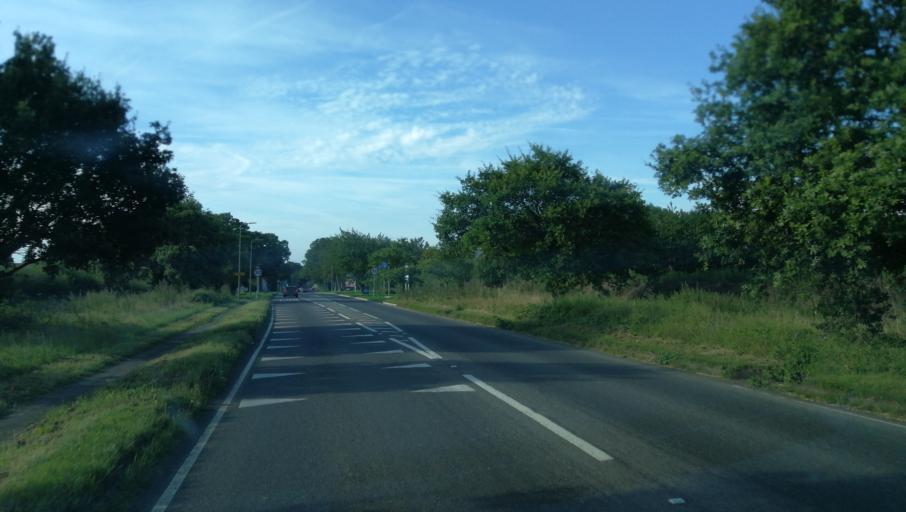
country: GB
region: England
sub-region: Oxfordshire
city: Deddington
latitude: 51.9858
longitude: -1.3224
